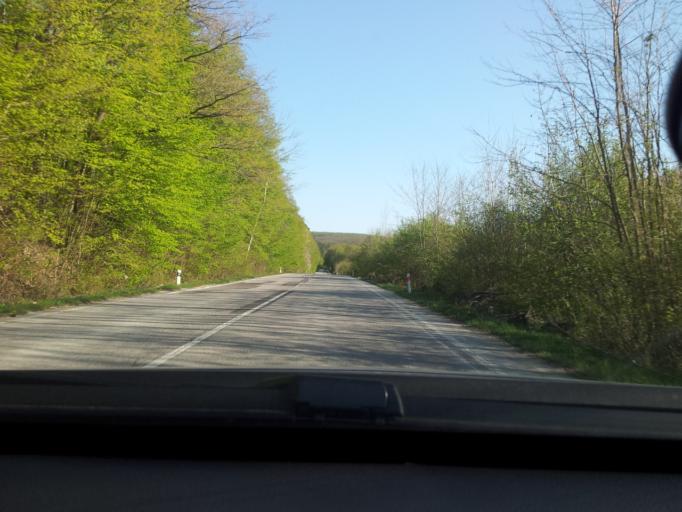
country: SK
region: Nitriansky
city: Zlate Moravce
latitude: 48.4660
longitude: 18.4124
